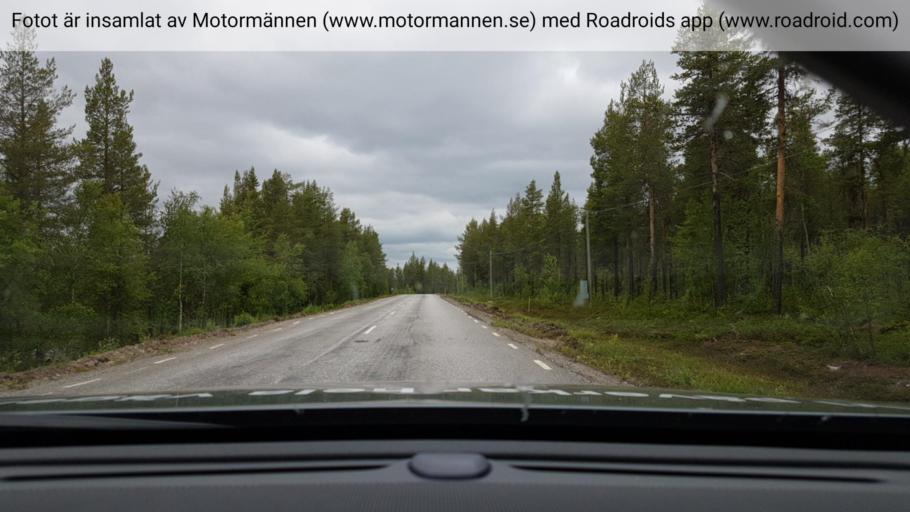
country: SE
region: Vaesterbotten
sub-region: Sorsele Kommun
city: Sorsele
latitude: 65.7643
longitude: 17.0654
